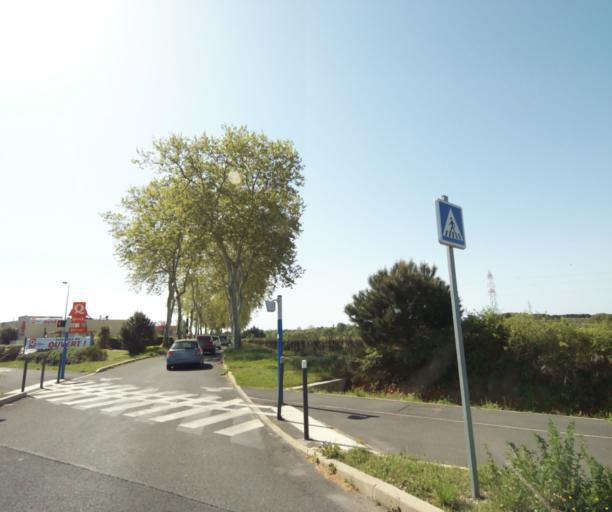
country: FR
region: Languedoc-Roussillon
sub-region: Departement de l'Herault
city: Perols
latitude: 43.5794
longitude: 3.9322
